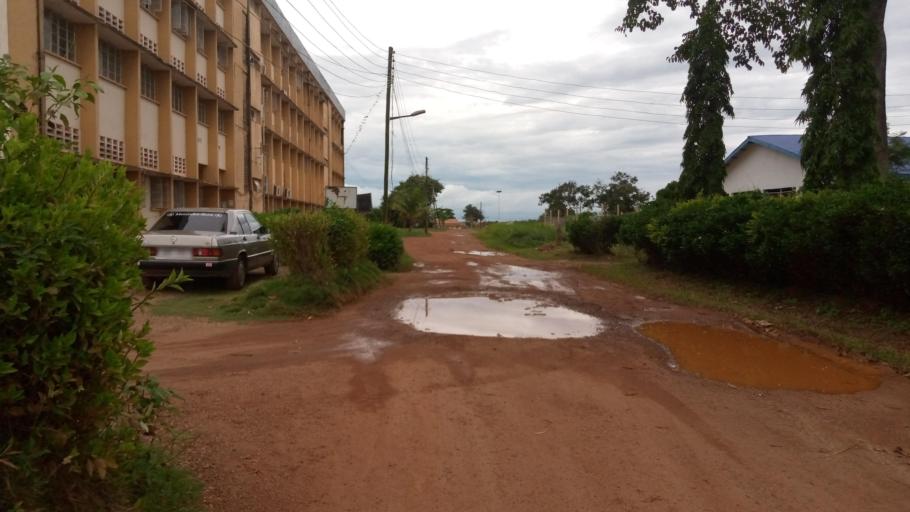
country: SL
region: Southern Province
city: Largo
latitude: 8.1176
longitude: -12.0691
